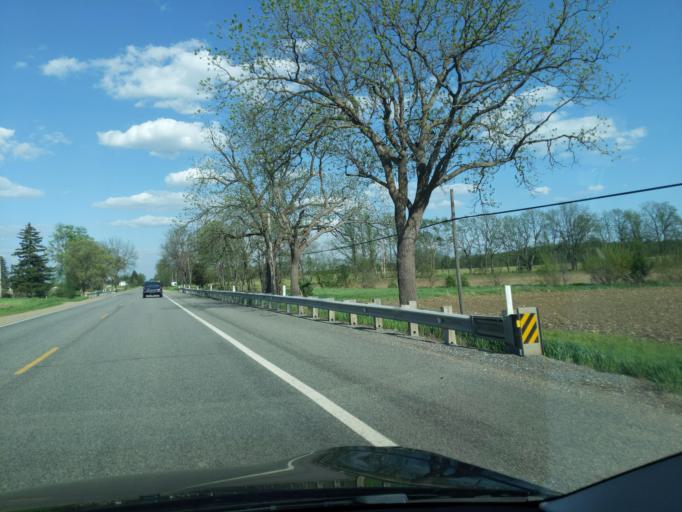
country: US
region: Michigan
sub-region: Eaton County
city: Grand Ledge
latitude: 42.7555
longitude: -84.7956
